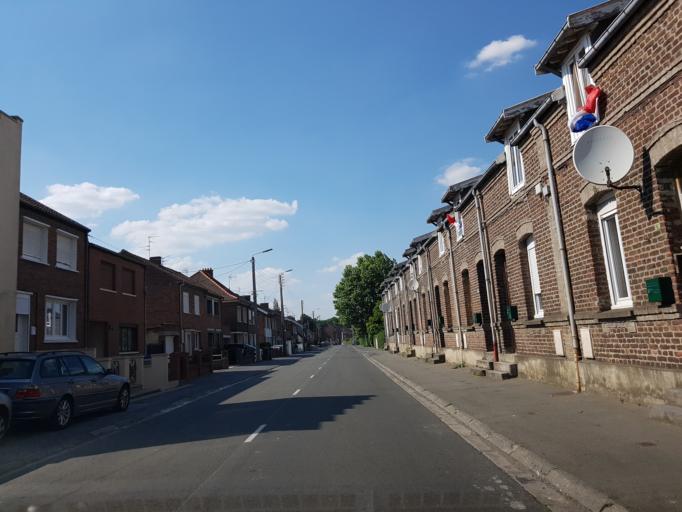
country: FR
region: Nord-Pas-de-Calais
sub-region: Departement du Nord
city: Lourches
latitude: 50.3144
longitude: 3.3437
